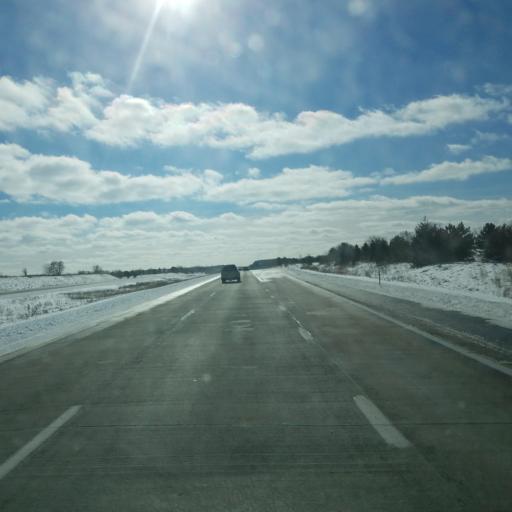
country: US
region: Michigan
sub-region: Clinton County
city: DeWitt
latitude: 42.8638
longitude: -84.5190
